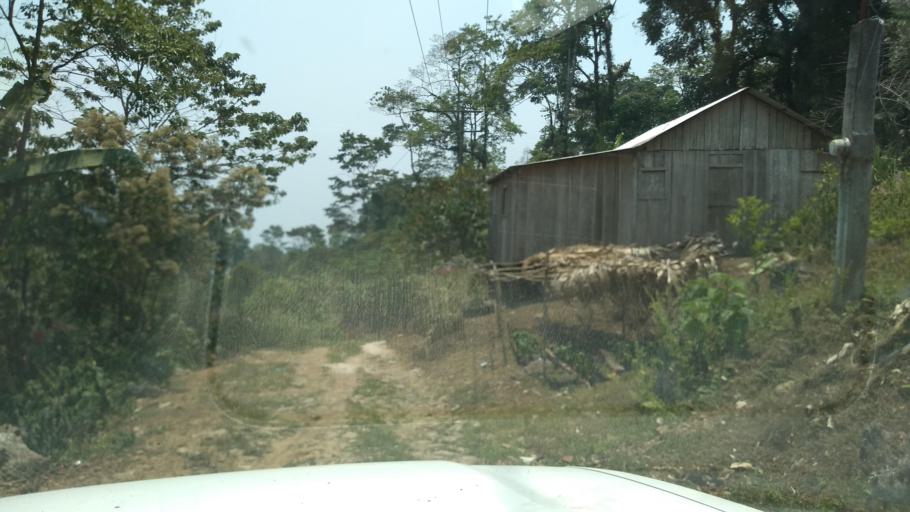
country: MX
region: Veracruz
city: Motzorongo
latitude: 18.6038
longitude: -96.7536
